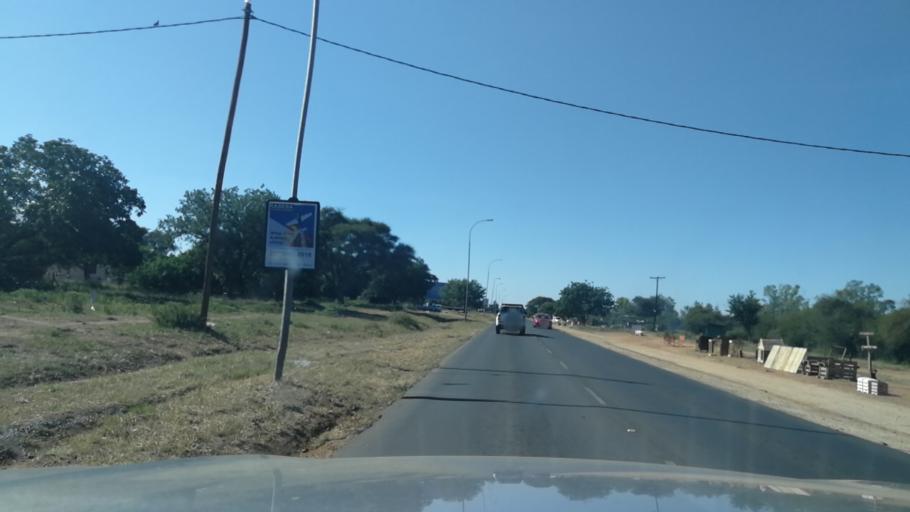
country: BW
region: South East
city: Gaborone
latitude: -24.6951
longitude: 25.8947
